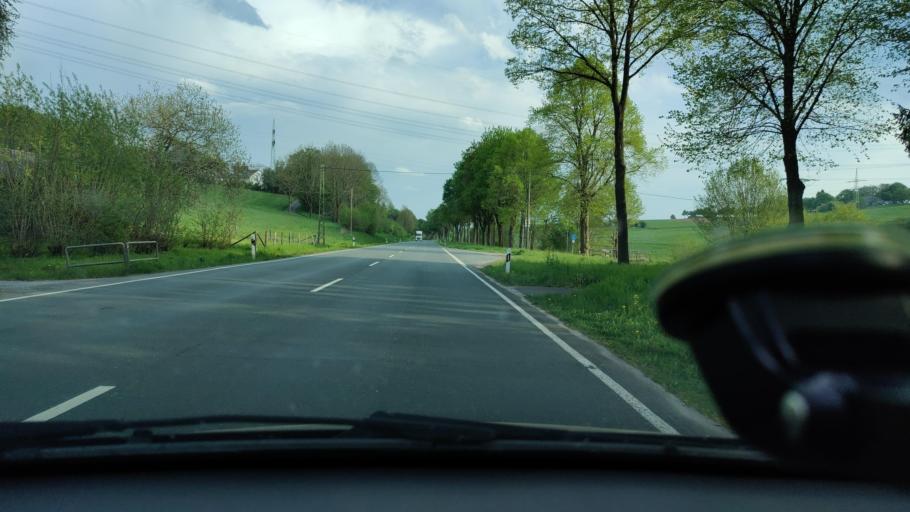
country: DE
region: North Rhine-Westphalia
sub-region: Regierungsbezirk Arnsberg
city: Brilon
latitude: 51.4299
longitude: 8.5743
